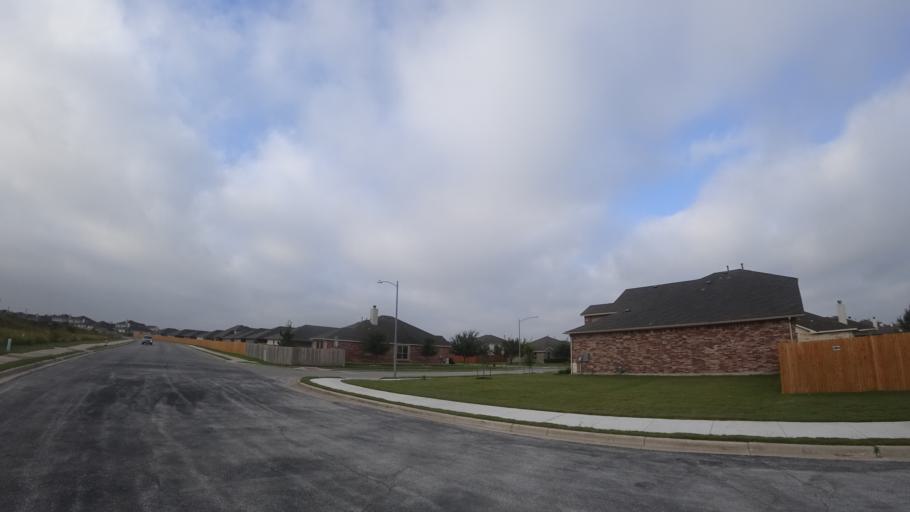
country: US
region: Texas
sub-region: Travis County
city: Pflugerville
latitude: 30.3643
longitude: -97.6417
